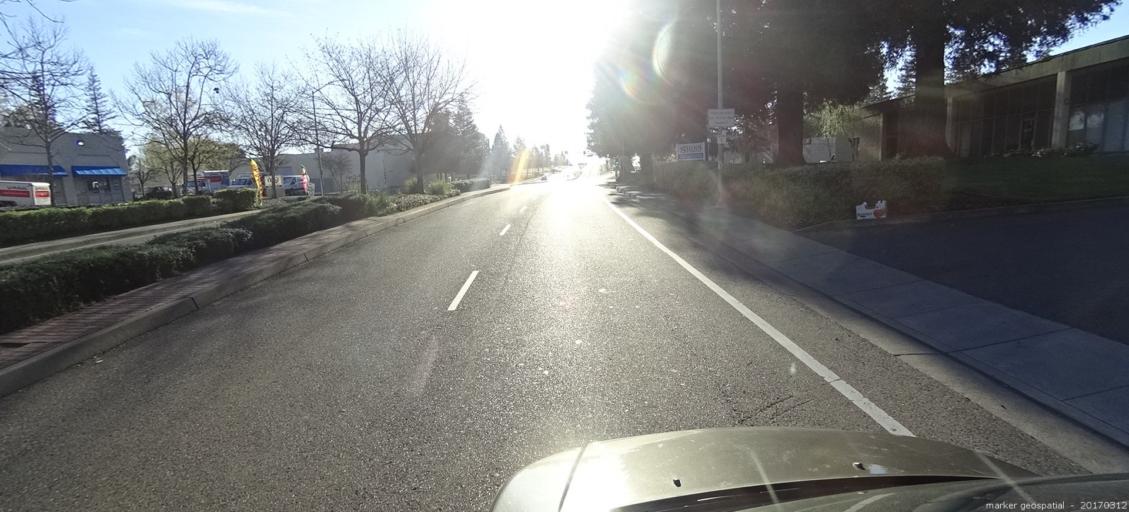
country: US
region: California
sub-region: Sacramento County
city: Sacramento
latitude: 38.5982
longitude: -121.4484
